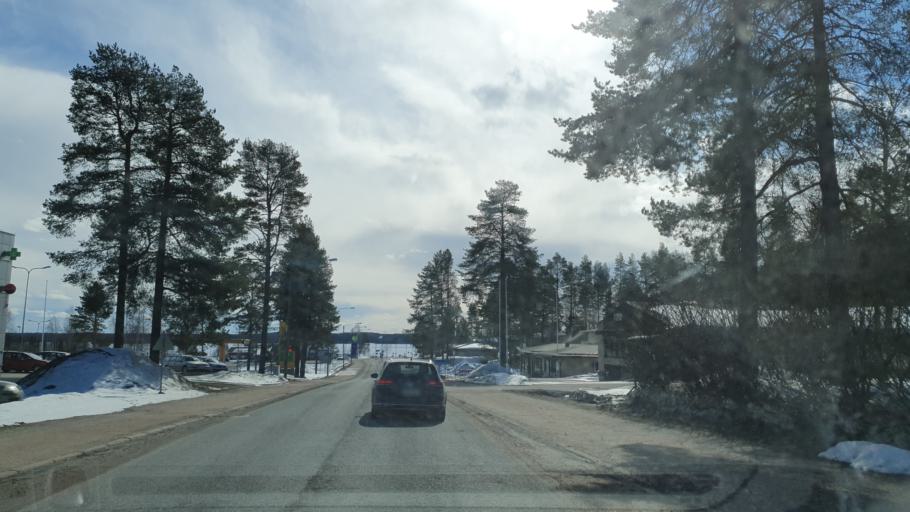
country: FI
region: Kainuu
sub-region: Kajaani
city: Paltamo
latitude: 64.4069
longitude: 27.8386
